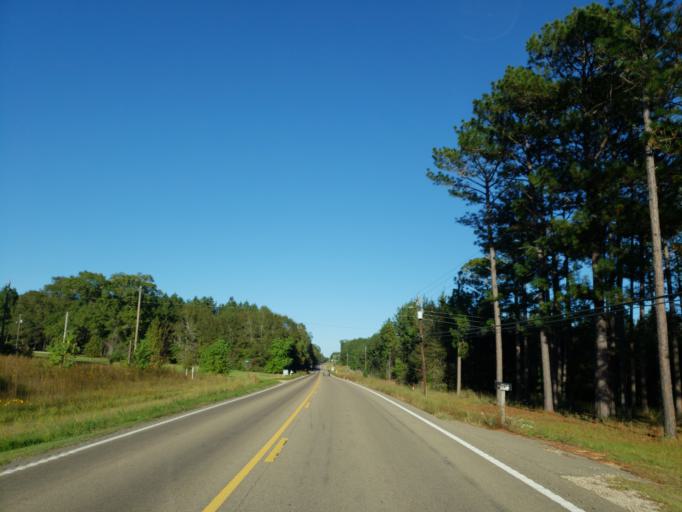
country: US
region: Mississippi
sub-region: Perry County
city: Richton
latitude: 31.3688
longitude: -88.8736
